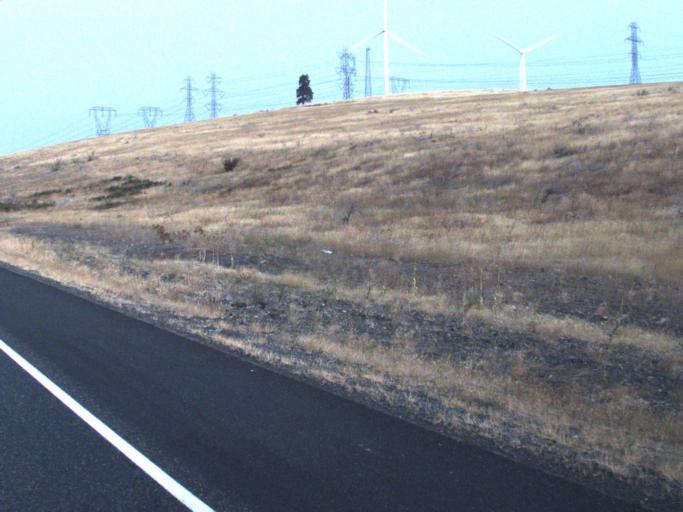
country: US
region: Washington
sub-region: Kittitas County
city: Ellensburg
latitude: 47.1254
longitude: -120.6773
